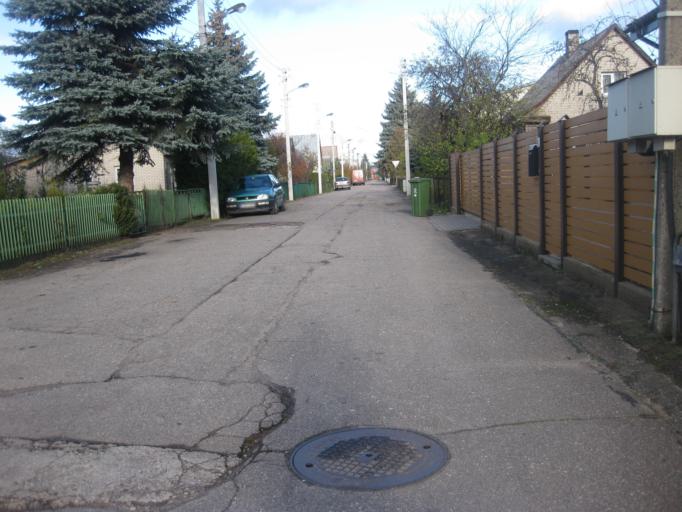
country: LT
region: Kauno apskritis
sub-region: Kaunas
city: Kaunas
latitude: 54.9157
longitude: 23.8956
